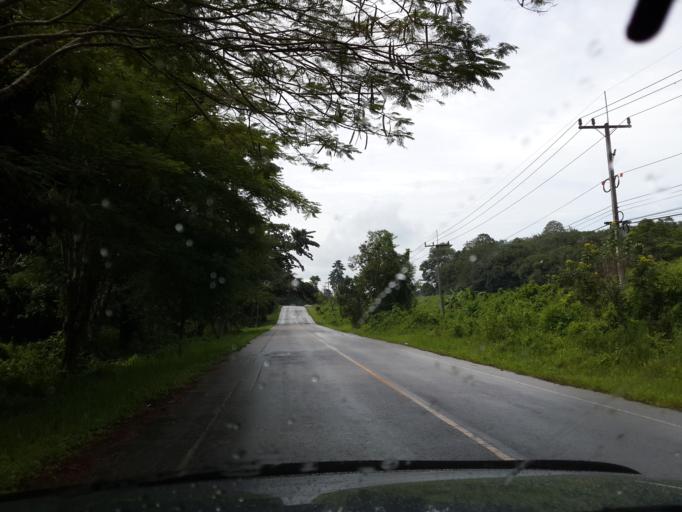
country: TH
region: Narathiwat
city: Rueso
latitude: 6.3684
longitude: 101.5335
